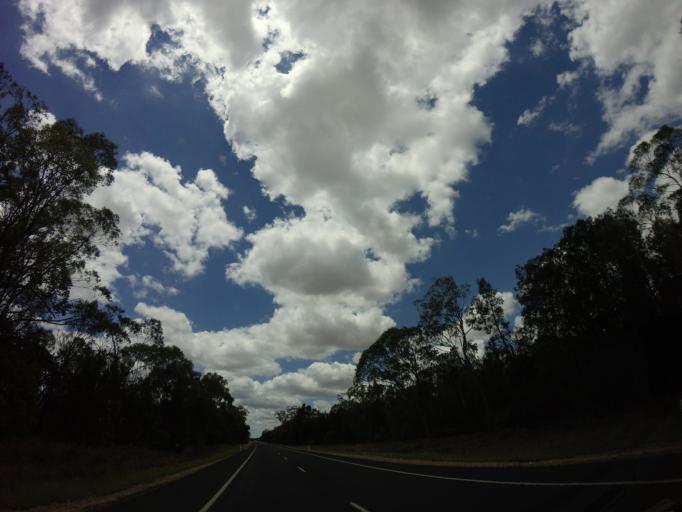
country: AU
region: Queensland
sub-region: Goondiwindi
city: Goondiwindi
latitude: -28.1150
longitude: 150.7142
